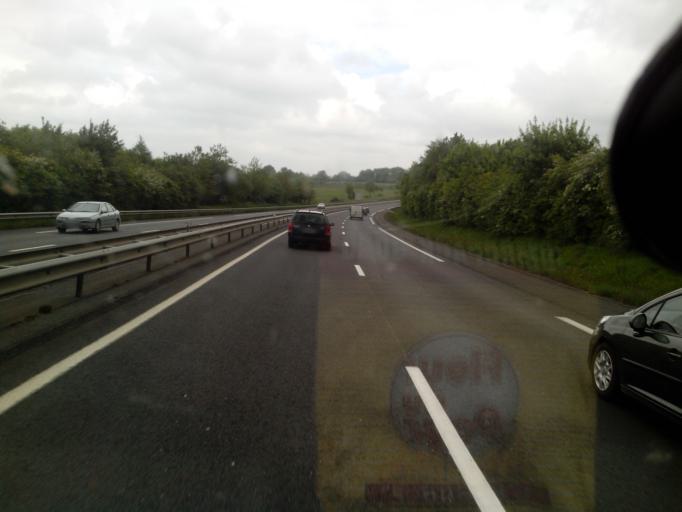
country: FR
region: Lower Normandy
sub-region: Departement du Calvados
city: Saint-Martin-des-Besaces
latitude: 49.0086
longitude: -0.8986
